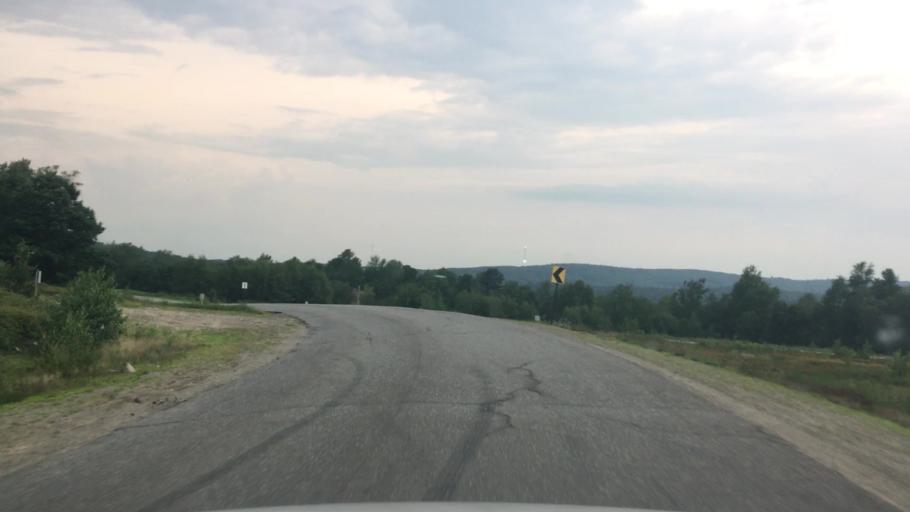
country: US
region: Maine
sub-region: Knox County
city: Washington
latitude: 44.3683
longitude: -69.3420
